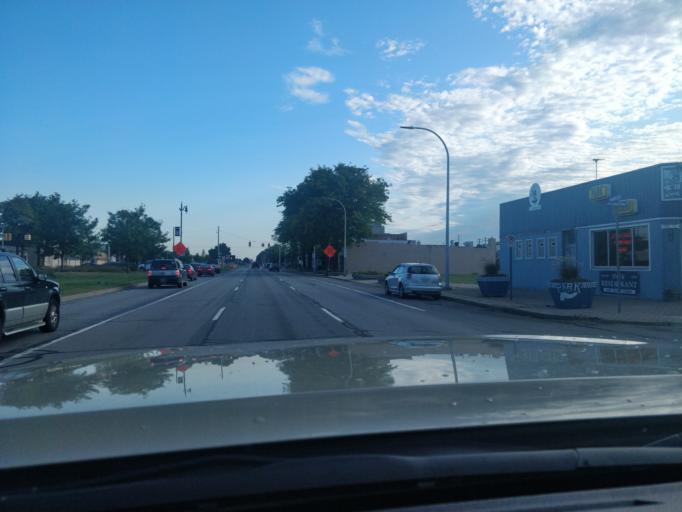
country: US
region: Michigan
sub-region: Wayne County
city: Lincoln Park
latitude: 42.2513
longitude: -83.1759
